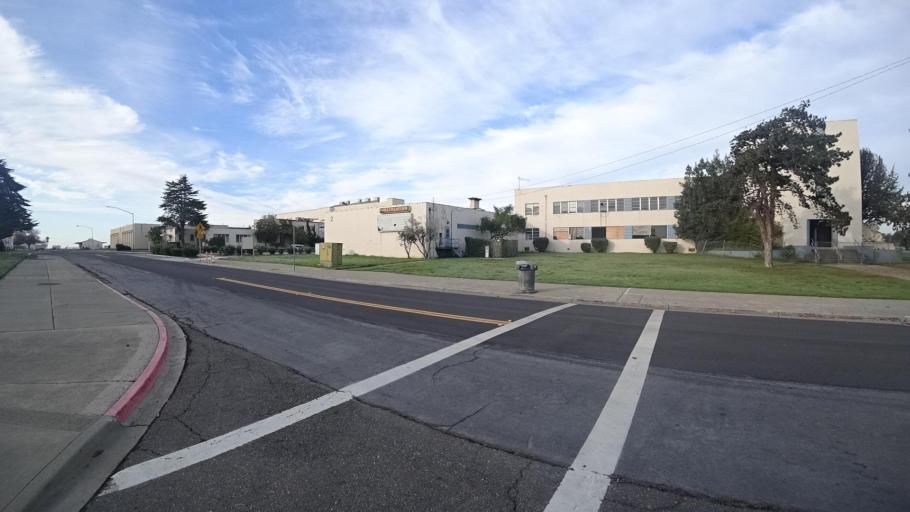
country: US
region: California
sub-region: Alameda County
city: Oakland
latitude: 37.7866
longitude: -122.3035
